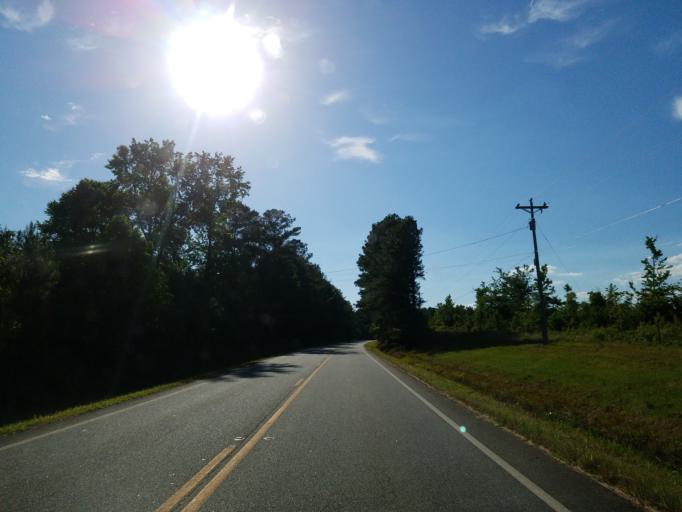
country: US
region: Georgia
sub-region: Gordon County
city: Calhoun
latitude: 34.5769
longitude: -84.9917
